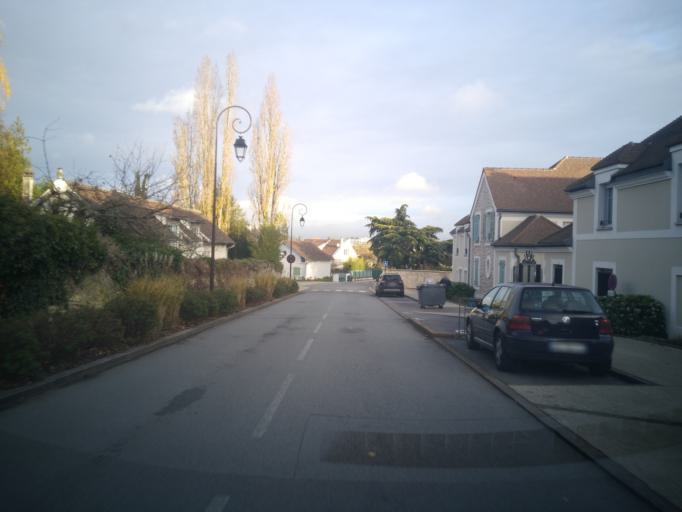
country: FR
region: Ile-de-France
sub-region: Departement des Yvelines
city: Fourqueux
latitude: 48.8881
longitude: 2.0633
